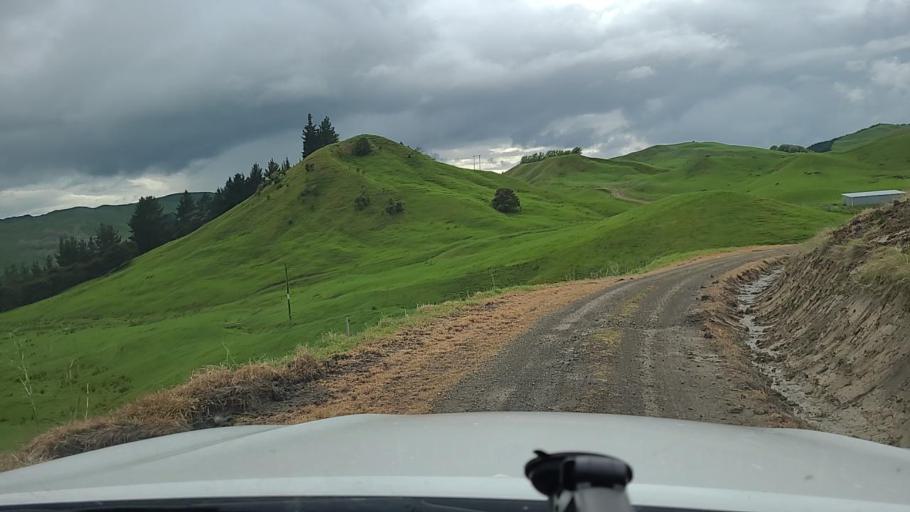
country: NZ
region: Gisborne
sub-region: Gisborne District
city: Gisborne
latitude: -38.4379
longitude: 177.7051
